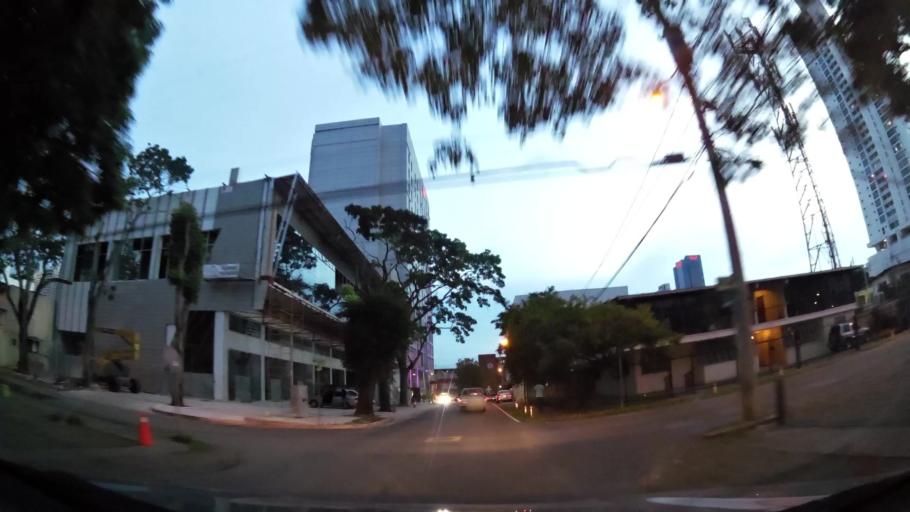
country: PA
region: Panama
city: Panama
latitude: 8.9884
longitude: -79.5076
